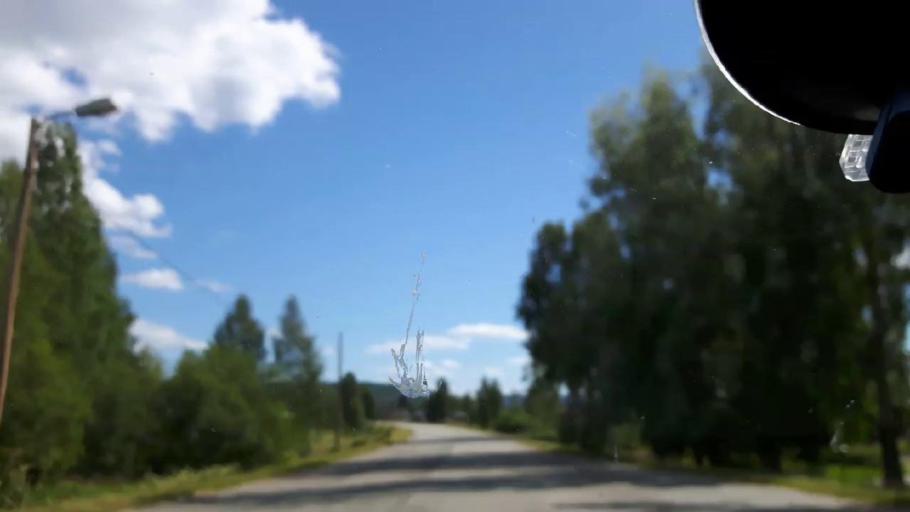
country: SE
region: Vaesternorrland
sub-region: Ange Kommun
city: Fransta
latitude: 62.7954
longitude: 16.2097
